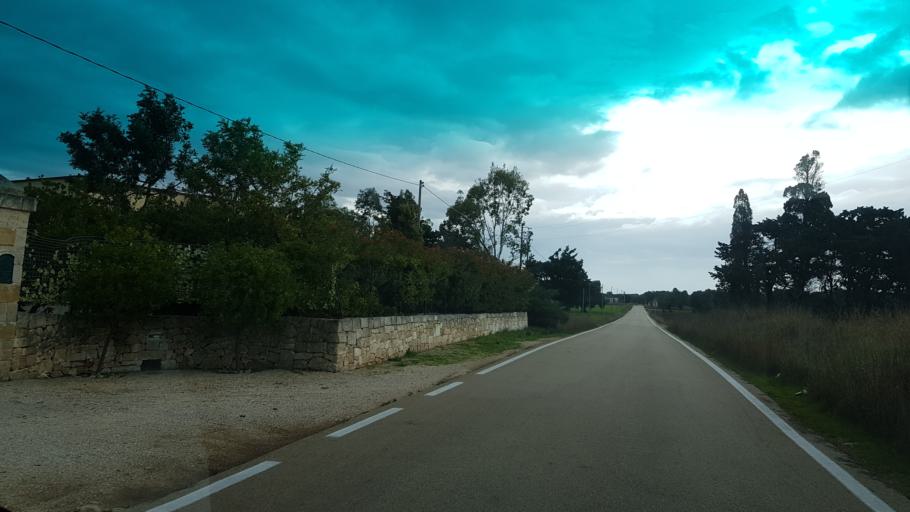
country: IT
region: Apulia
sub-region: Provincia di Brindisi
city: San Vito dei Normanni
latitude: 40.7130
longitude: 17.7655
